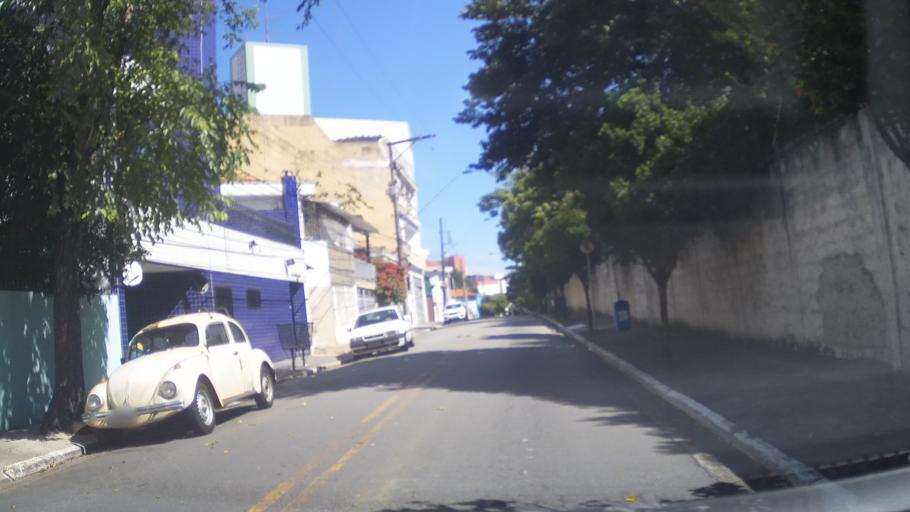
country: BR
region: Sao Paulo
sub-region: Sao Caetano Do Sul
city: Sao Caetano do Sul
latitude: -23.6370
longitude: -46.5717
